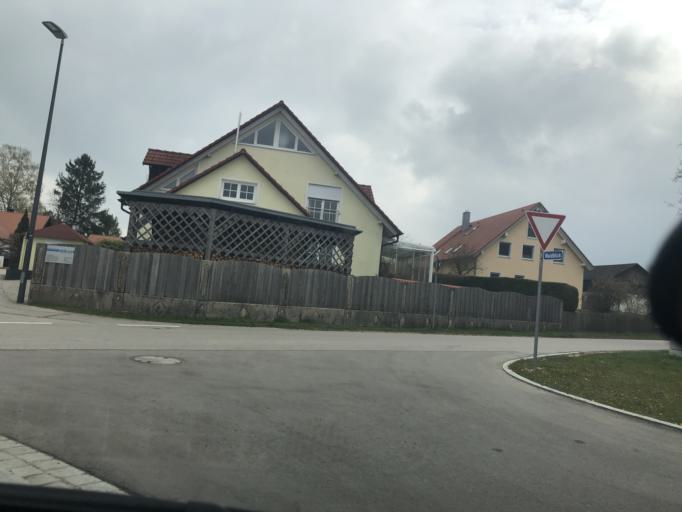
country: DE
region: Bavaria
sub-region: Upper Bavaria
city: Kirchdorf
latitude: 48.4392
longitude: 11.6808
